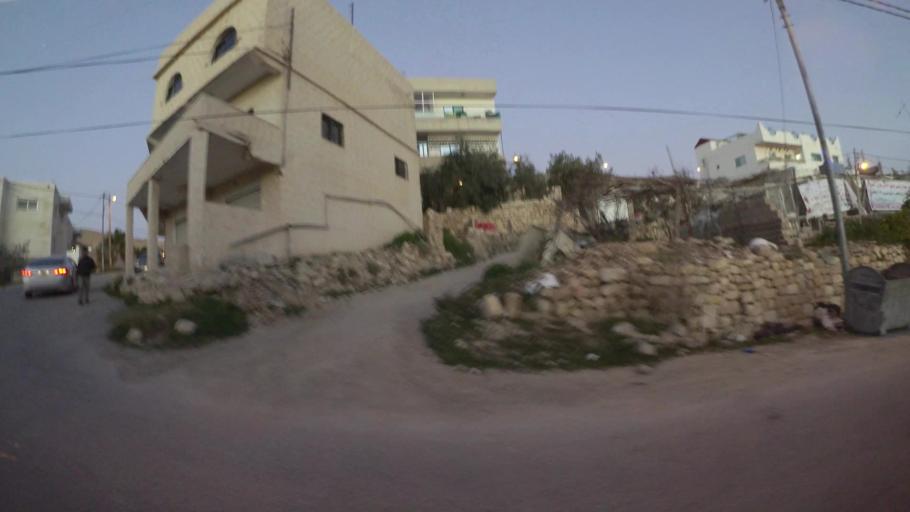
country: JO
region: Ma'an
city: Petra
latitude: 30.3240
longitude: 35.4803
